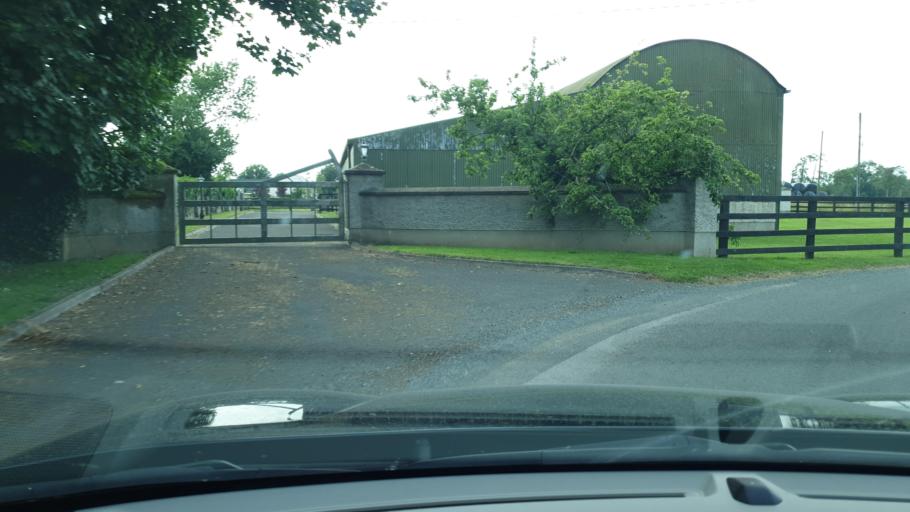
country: IE
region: Leinster
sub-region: An Mhi
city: Ratoath
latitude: 53.4674
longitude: -6.4369
